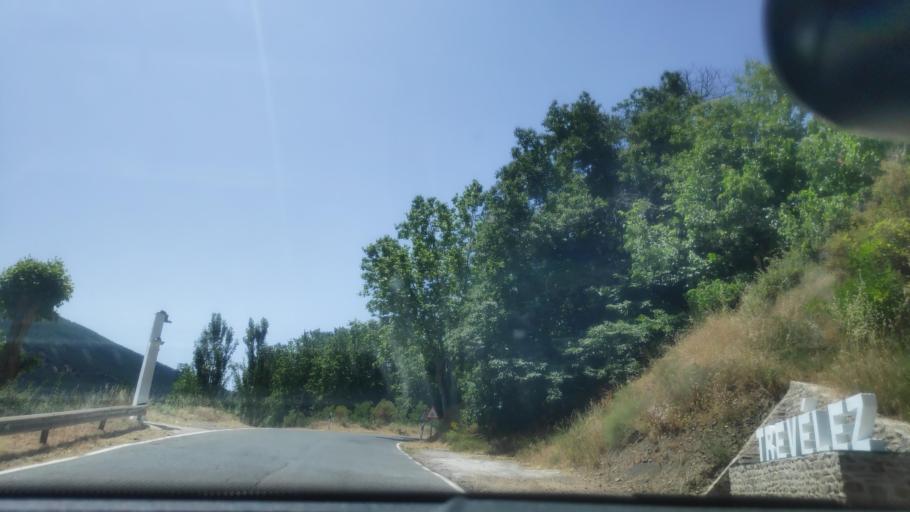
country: ES
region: Andalusia
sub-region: Provincia de Granada
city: Trevelez
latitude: 36.9953
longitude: -3.2700
